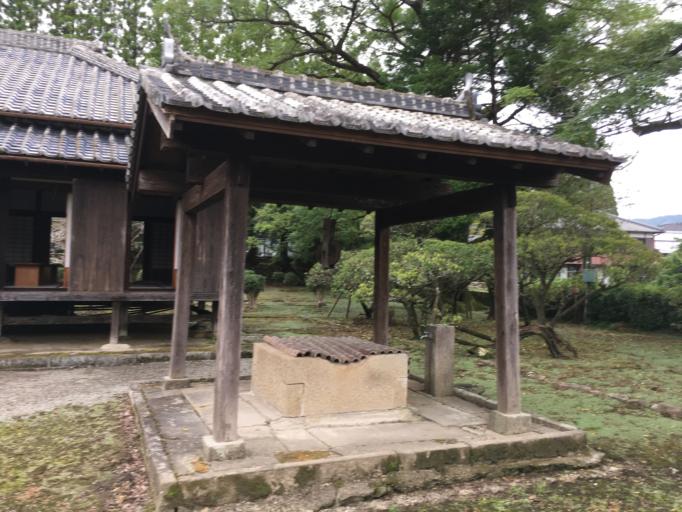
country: JP
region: Miyazaki
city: Nichinan
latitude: 31.6293
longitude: 131.3545
